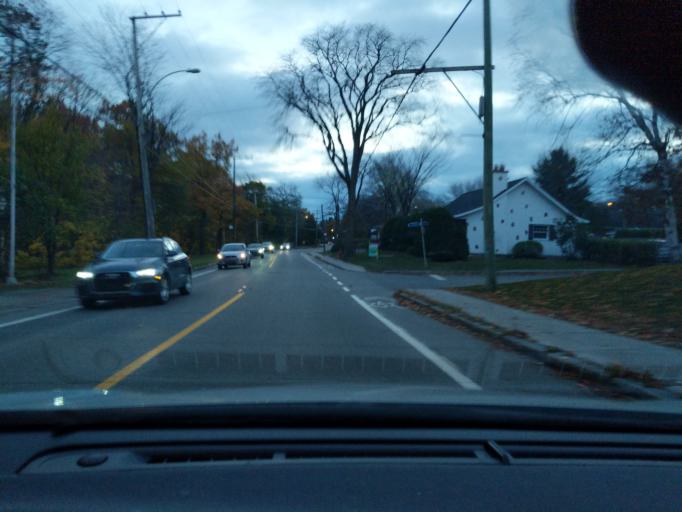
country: CA
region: Quebec
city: Quebec
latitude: 46.7738
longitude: -71.2558
